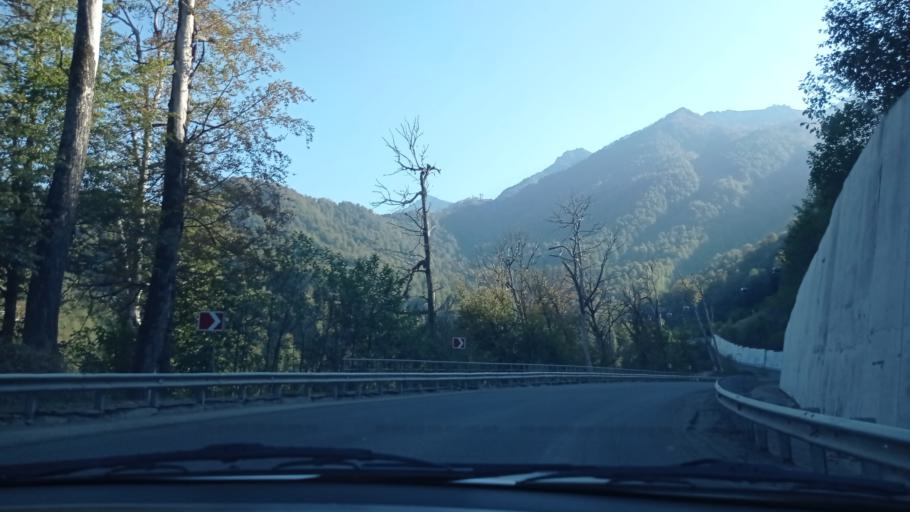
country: RU
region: Krasnodarskiy
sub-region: Sochi City
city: Krasnaya Polyana
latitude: 43.6658
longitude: 40.3000
